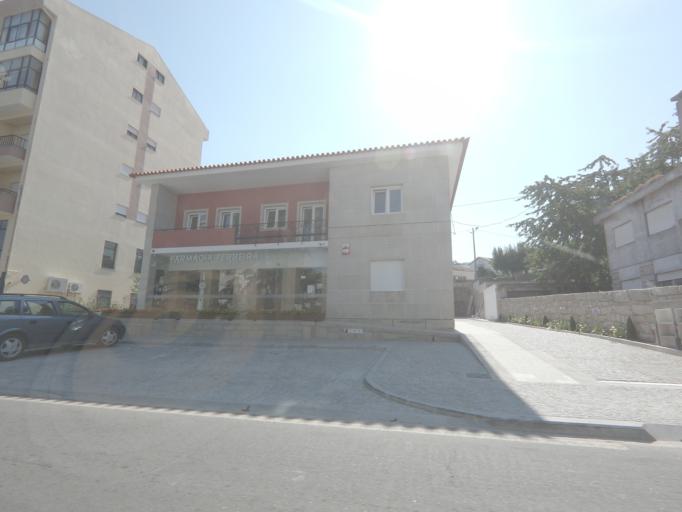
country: PT
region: Viseu
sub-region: Moimenta da Beira
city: Moimenta da Beira
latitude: 40.9787
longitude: -7.6128
